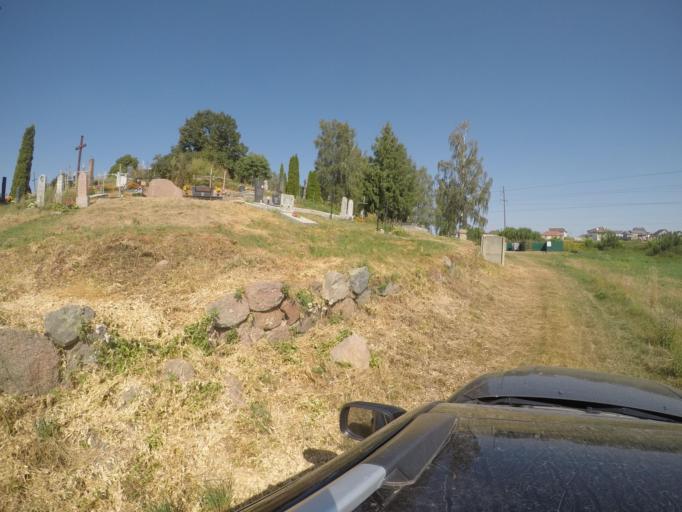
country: BY
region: Grodnenskaya
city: Hrodna
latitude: 53.7111
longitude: 23.8790
